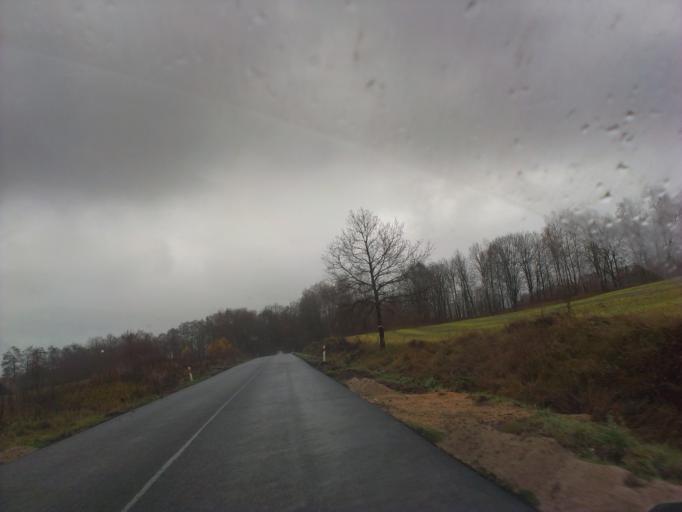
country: PL
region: West Pomeranian Voivodeship
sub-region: Powiat szczecinecki
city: Borne Sulinowo
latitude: 53.6264
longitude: 16.5103
